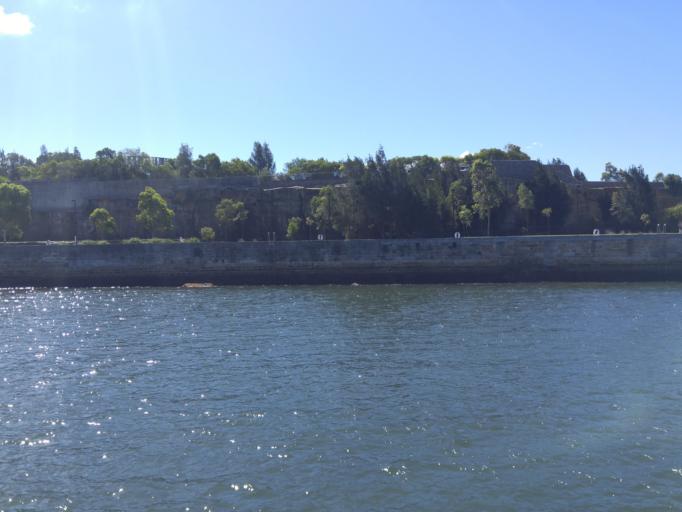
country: AU
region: New South Wales
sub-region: Leichhardt
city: Balmain East
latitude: -33.8530
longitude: 151.1905
